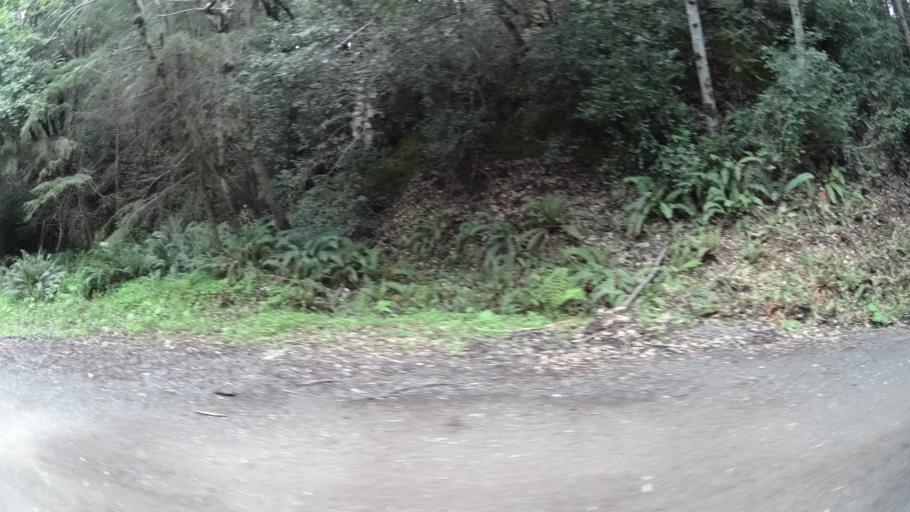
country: US
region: California
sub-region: Humboldt County
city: Blue Lake
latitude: 40.7660
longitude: -123.9549
